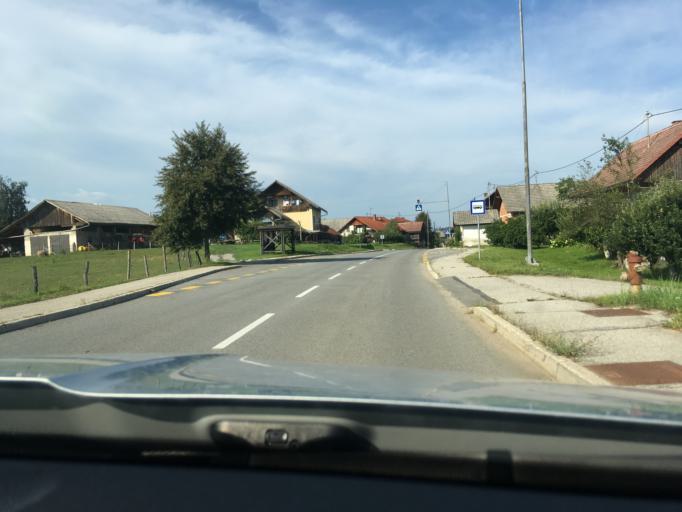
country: SI
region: Crnomelj
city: Crnomelj
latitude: 45.6001
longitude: 15.2315
